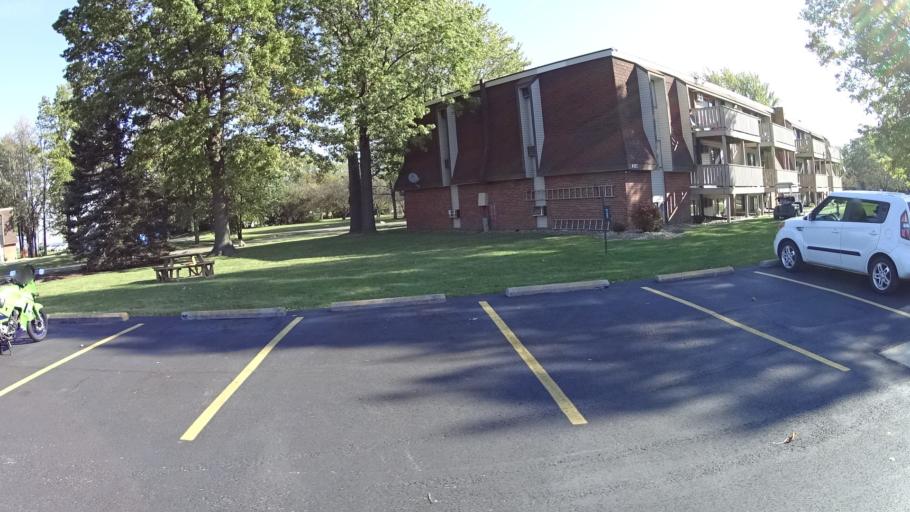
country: US
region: Ohio
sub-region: Lorain County
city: Vermilion
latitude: 41.4267
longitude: -82.3484
